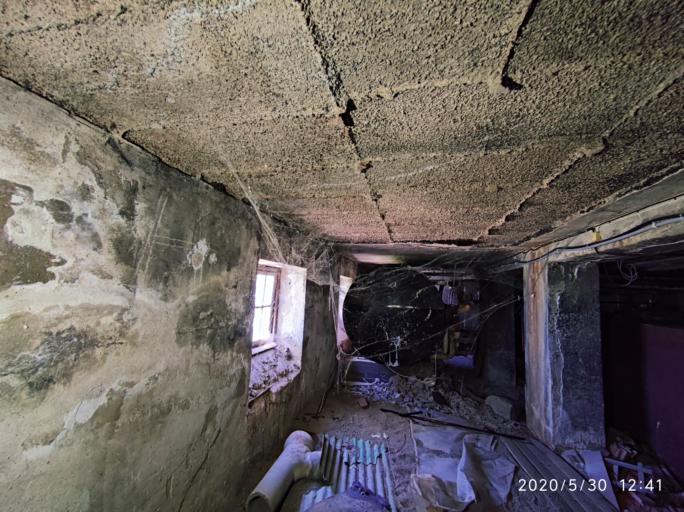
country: NO
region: Buskerud
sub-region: Lier
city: Tranby
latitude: 59.7919
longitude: 10.2649
